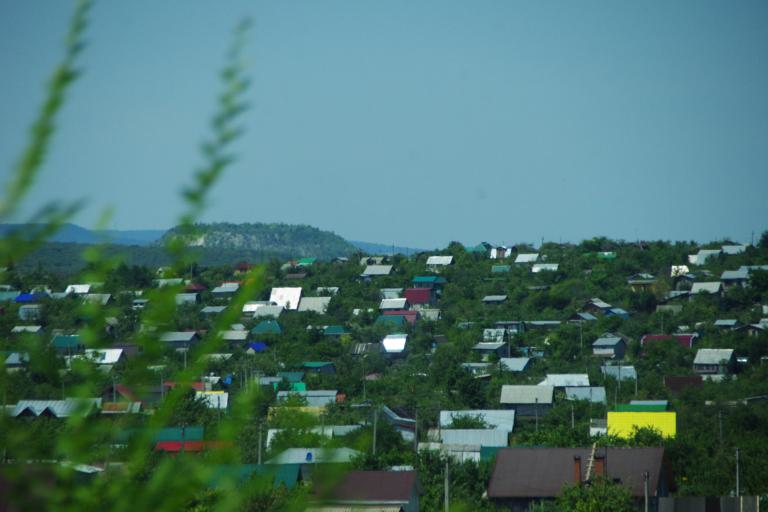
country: RU
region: Samara
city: Novosemeykino
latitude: 53.4072
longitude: 50.3358
